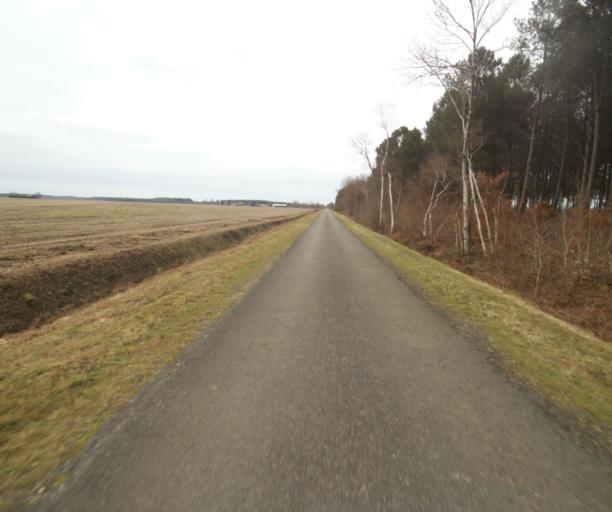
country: FR
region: Aquitaine
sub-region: Departement des Landes
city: Gabarret
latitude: 44.0324
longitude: -0.0639
